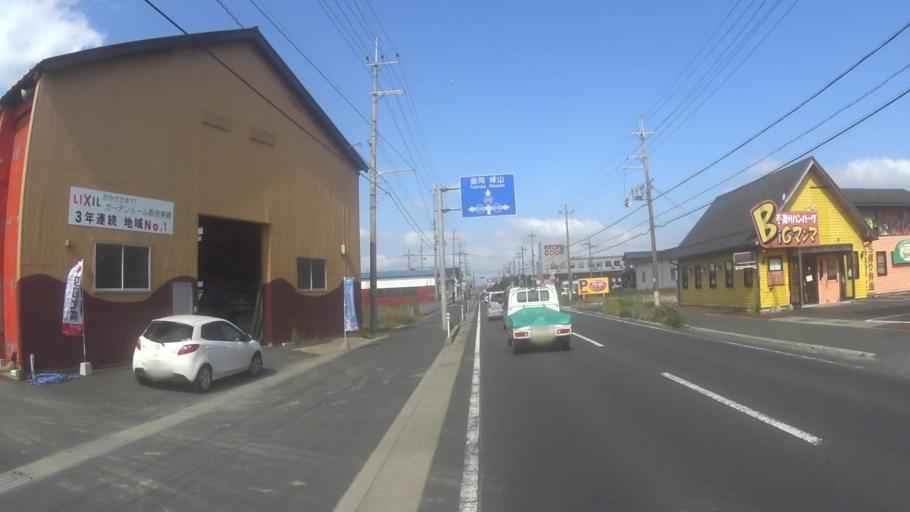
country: JP
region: Kyoto
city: Miyazu
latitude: 35.5978
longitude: 135.0887
